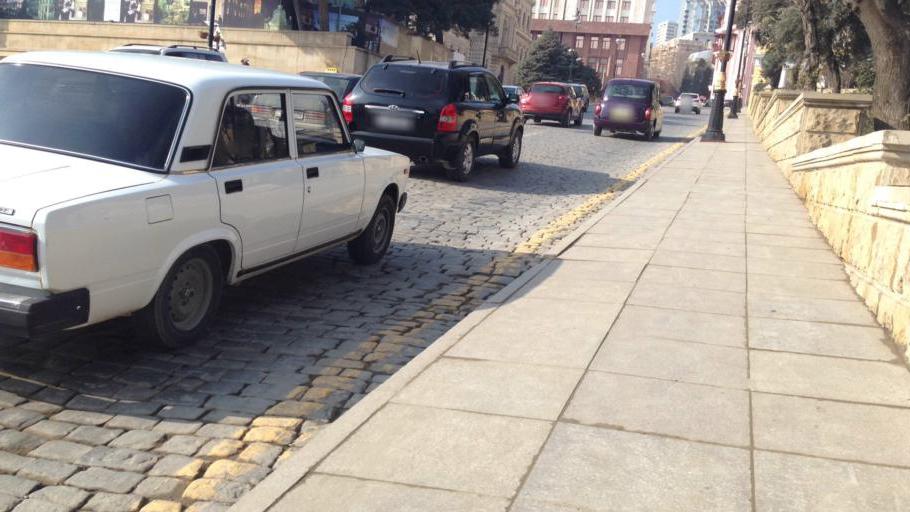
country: AZ
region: Baki
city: Badamdar
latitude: 40.3634
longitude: 49.8327
